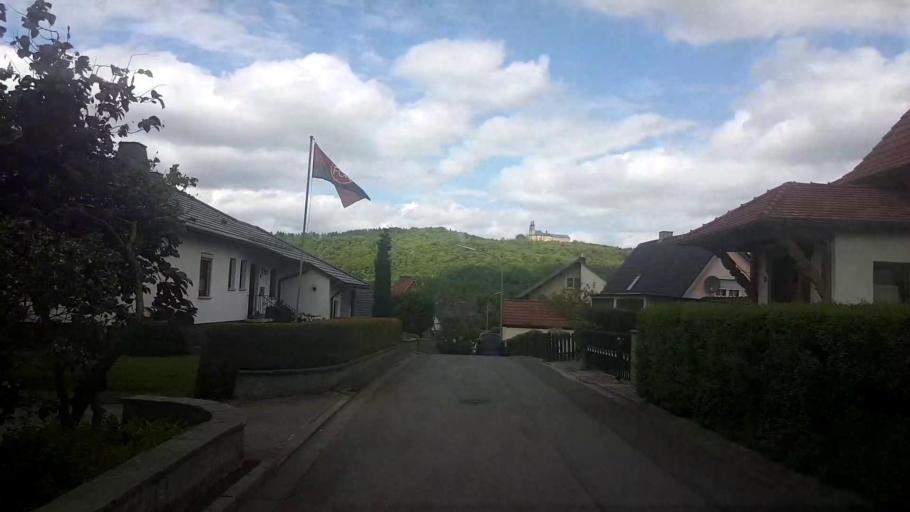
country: DE
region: Bavaria
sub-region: Upper Franconia
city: Bad Staffelstein
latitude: 50.1183
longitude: 11.0121
